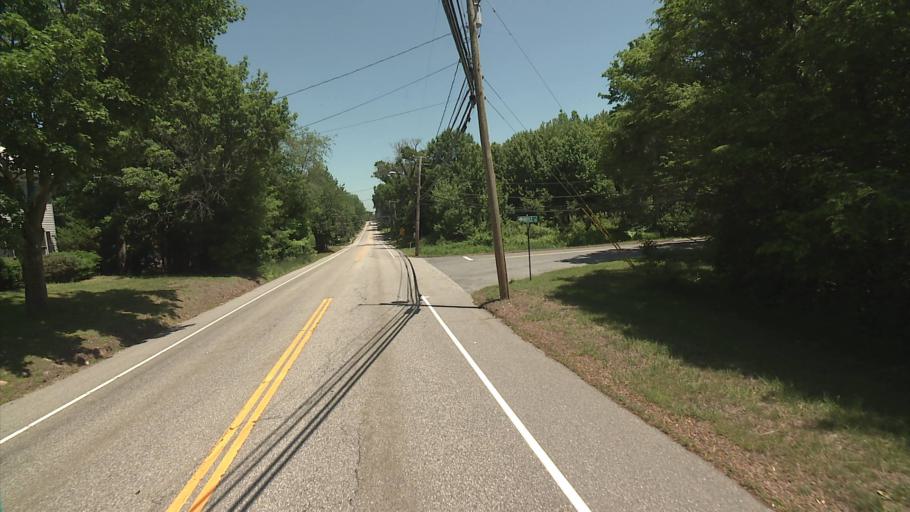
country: US
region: Connecticut
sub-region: Tolland County
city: Tolland
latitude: 41.8820
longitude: -72.4037
